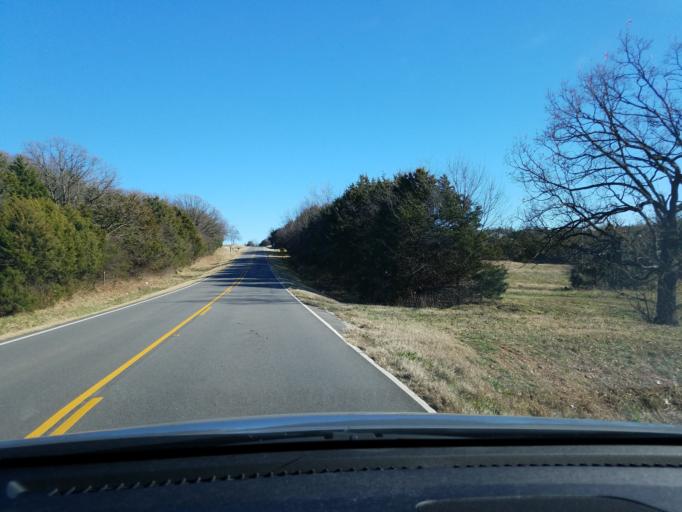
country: US
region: Arkansas
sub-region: Carroll County
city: Berryville
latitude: 36.4094
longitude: -93.5382
